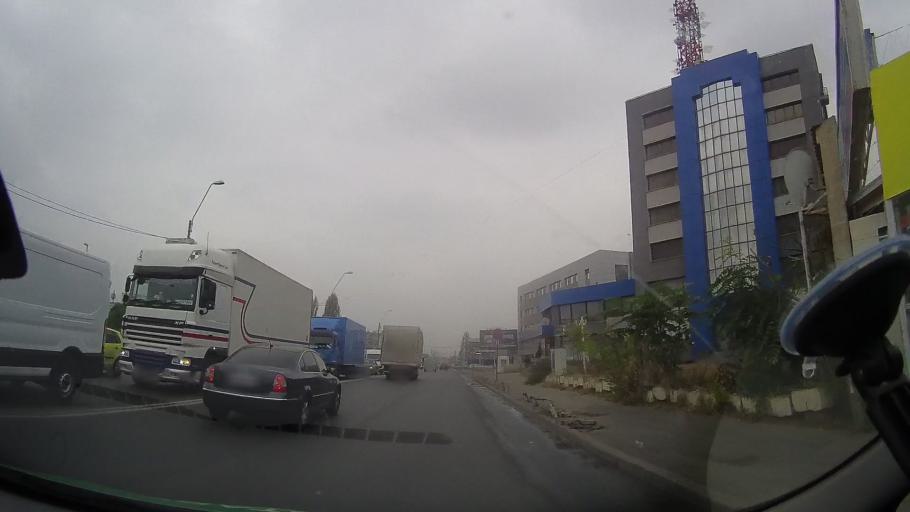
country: RO
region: Ilfov
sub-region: Comuna Chiajna
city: Rosu
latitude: 44.4307
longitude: 26.0038
